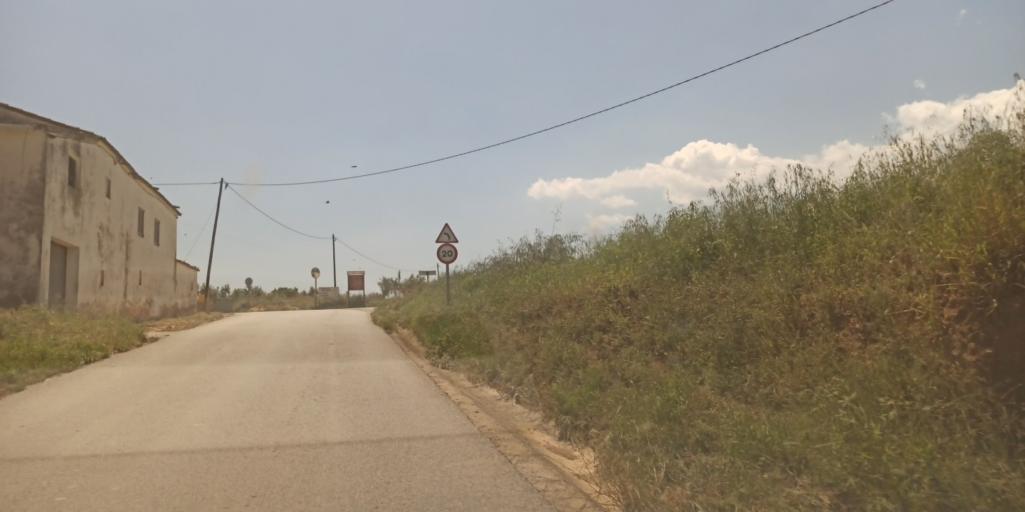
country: ES
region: Catalonia
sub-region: Provincia de Barcelona
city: Vilobi del Penedes
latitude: 41.3574
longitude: 1.6390
